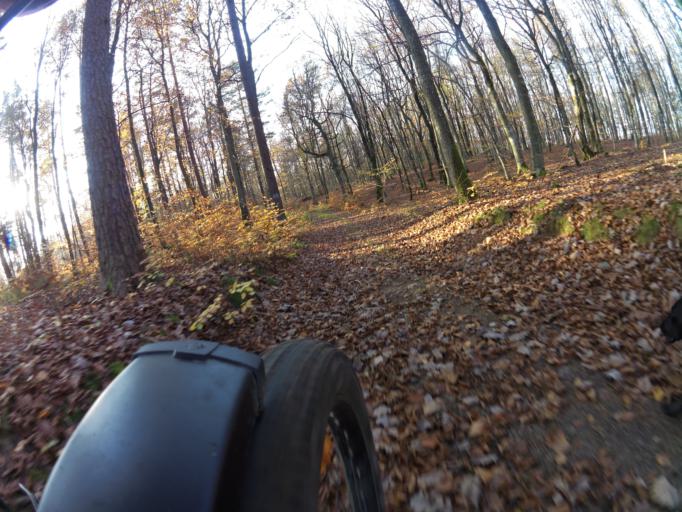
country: PL
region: Pomeranian Voivodeship
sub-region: Powiat pucki
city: Krokowa
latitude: 54.7295
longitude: 18.2035
